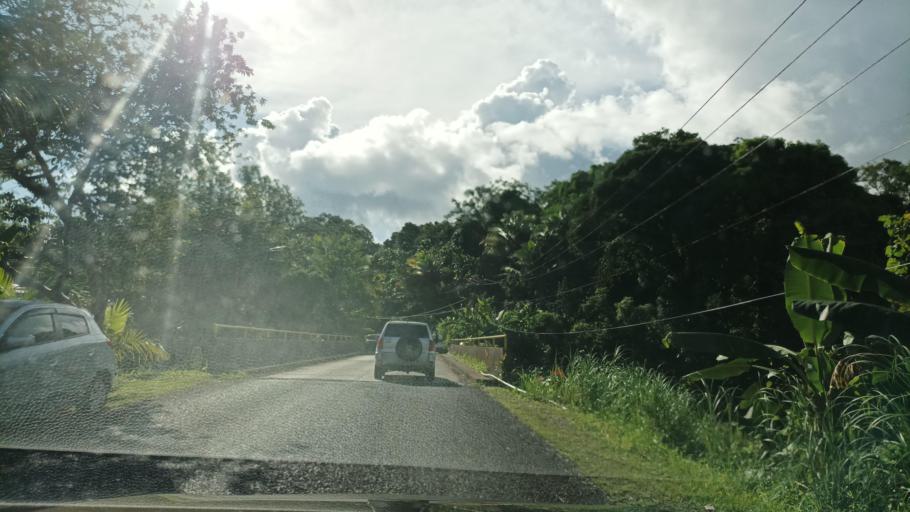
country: FM
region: Pohnpei
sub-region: Sokehs Municipality
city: Palikir - National Government Center
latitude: 6.8244
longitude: 158.1720
